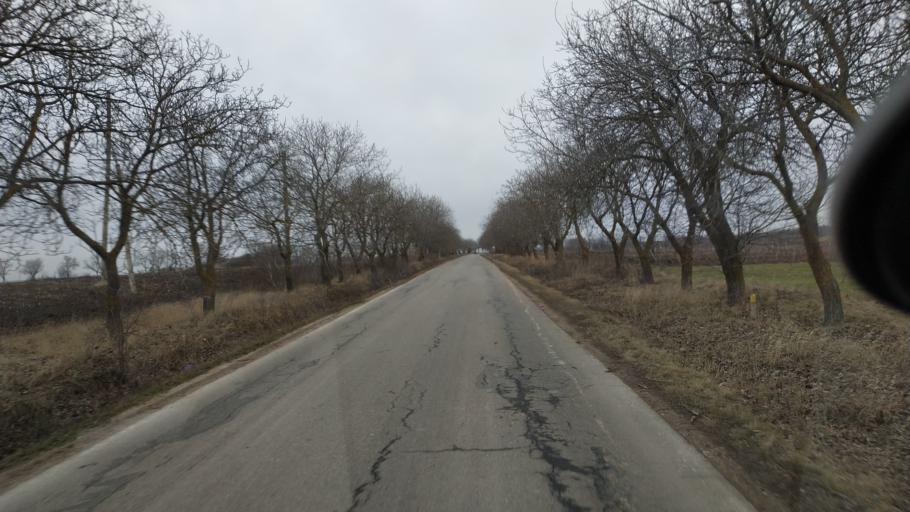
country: MD
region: Telenesti
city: Cocieri
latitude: 47.2986
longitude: 29.0640
